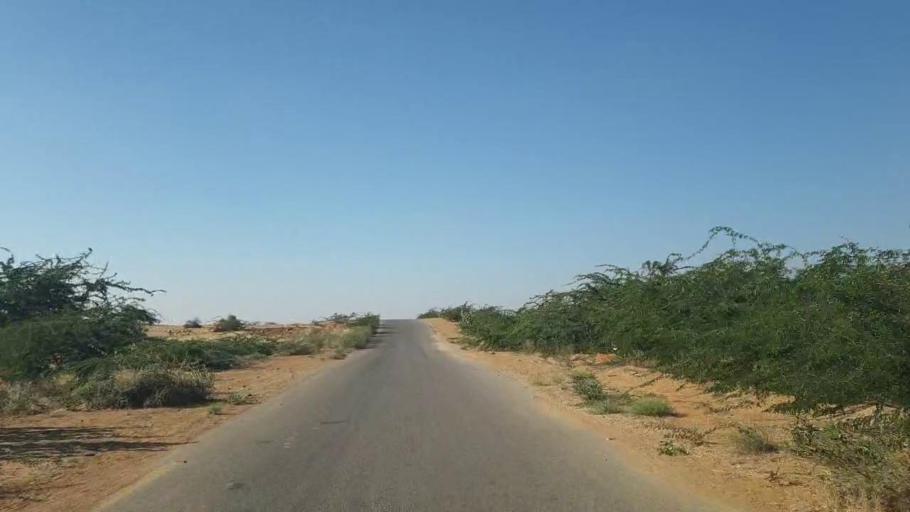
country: PK
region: Sindh
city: Malir Cantonment
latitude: 25.2813
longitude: 67.5831
